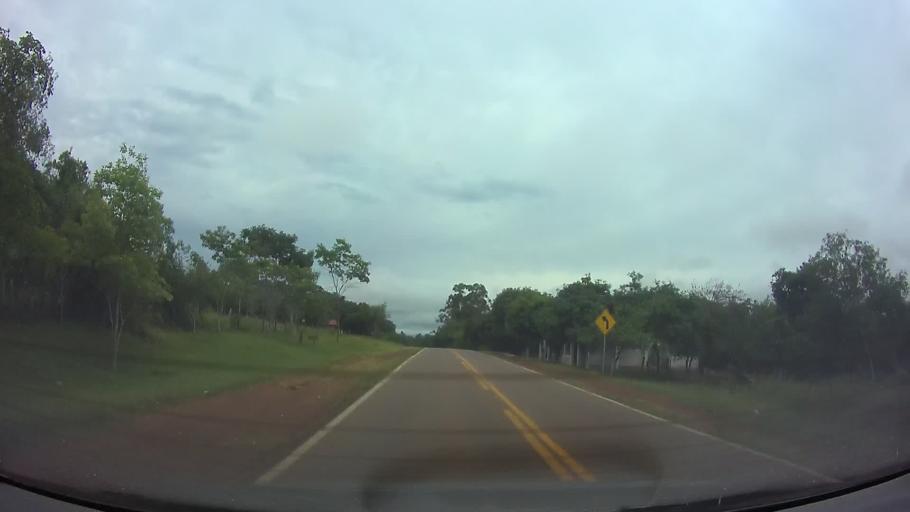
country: PY
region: Paraguari
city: Acahay
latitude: -25.8677
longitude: -57.1272
